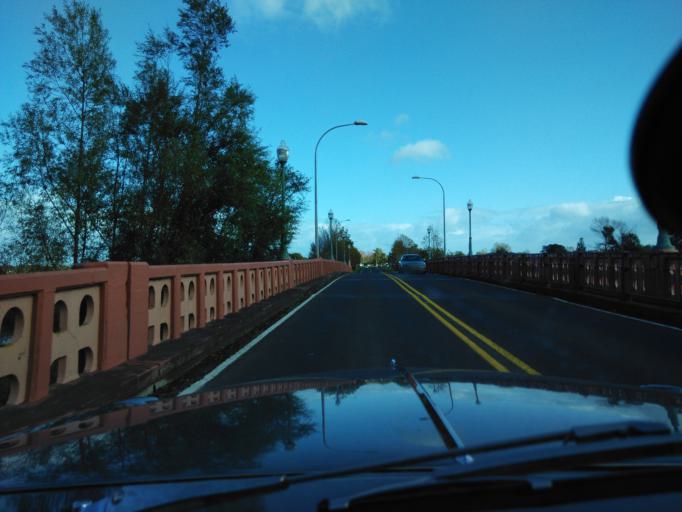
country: NZ
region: Waikato
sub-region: Hauraki District
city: Paeroa
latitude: -37.5459
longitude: 175.7082
